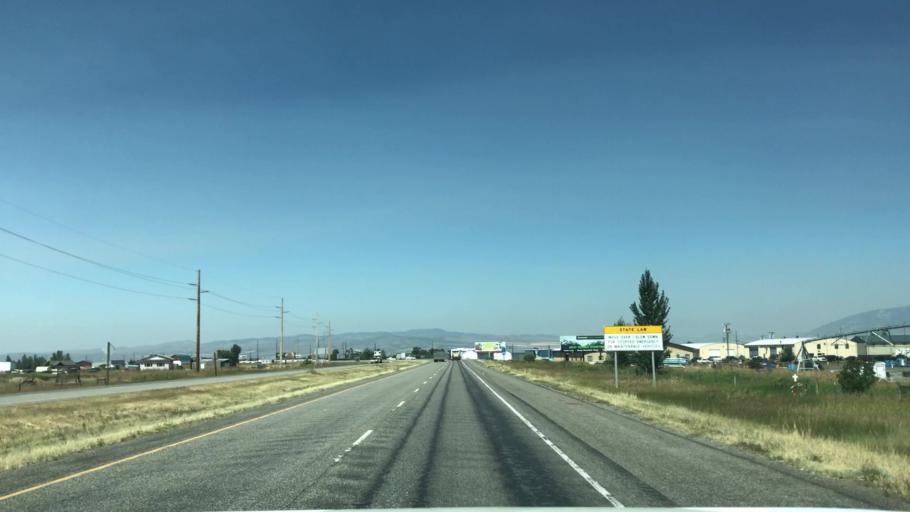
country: US
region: Montana
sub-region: Gallatin County
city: Belgrade
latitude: 45.7803
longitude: -111.2002
